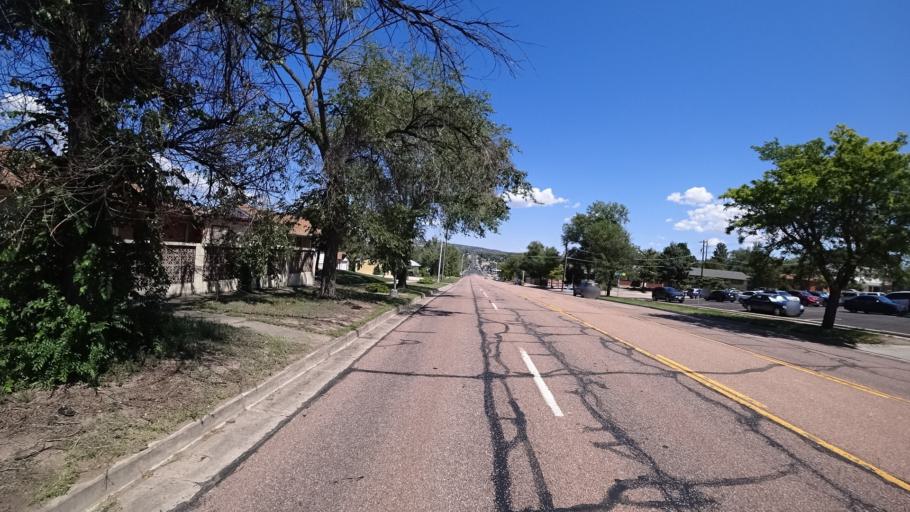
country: US
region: Colorado
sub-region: El Paso County
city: Colorado Springs
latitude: 38.8510
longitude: -104.7944
